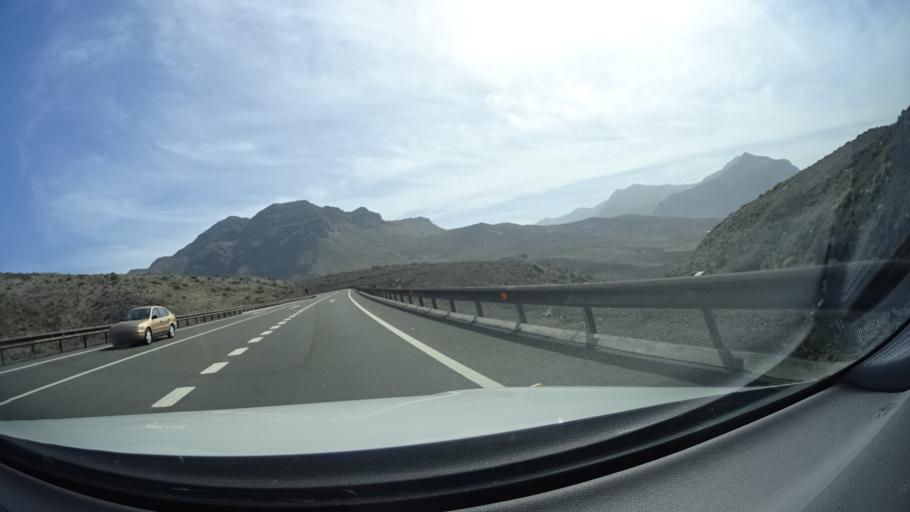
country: ES
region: Canary Islands
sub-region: Provincia de Las Palmas
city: San Nicolas
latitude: 28.0123
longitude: -15.7790
